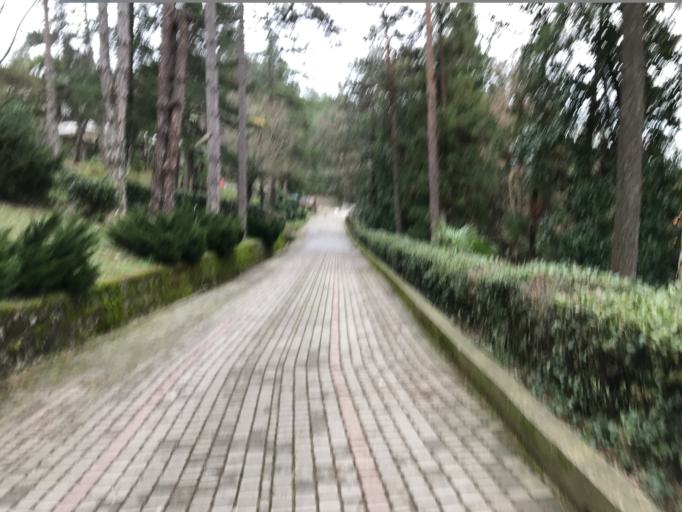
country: TR
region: Yalova
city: Termal
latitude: 40.6040
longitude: 29.1711
